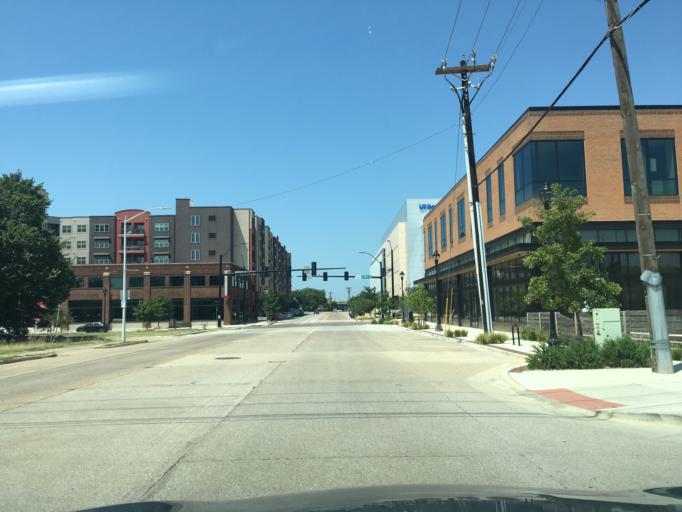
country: US
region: Texas
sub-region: Tarrant County
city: Fort Worth
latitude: 32.7380
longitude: -97.3250
